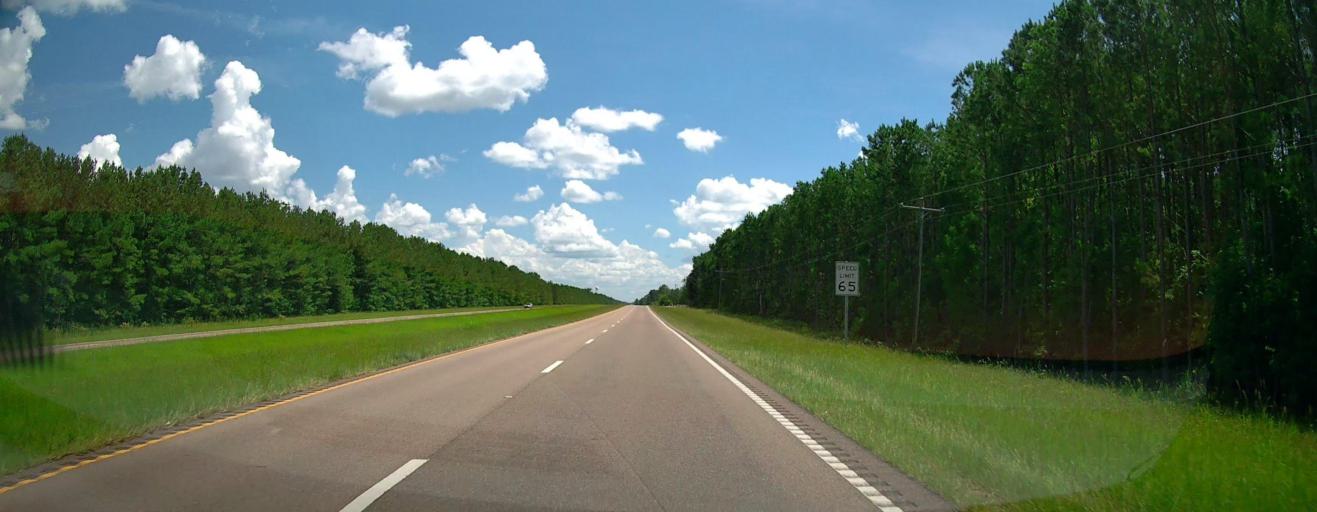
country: US
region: Mississippi
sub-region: Monroe County
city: Aberdeen
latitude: 33.9134
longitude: -88.5963
